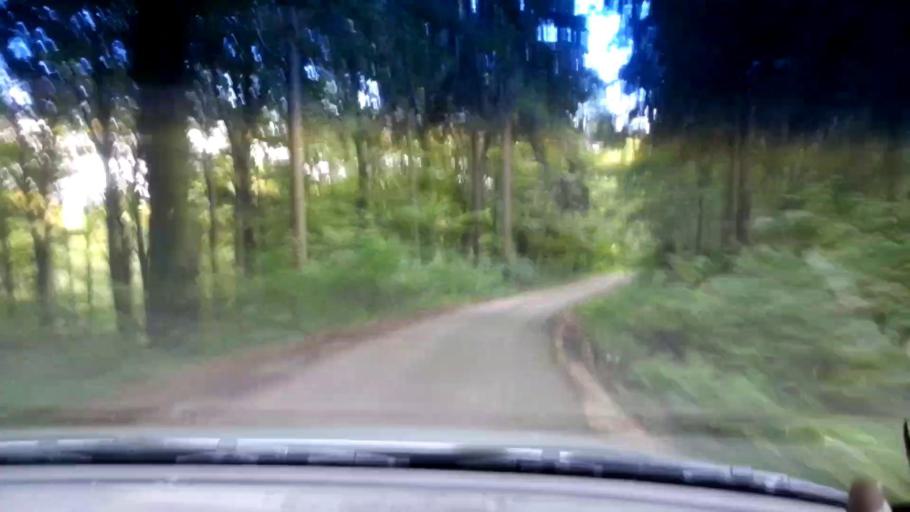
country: DE
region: Bavaria
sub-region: Upper Franconia
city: Schesslitz
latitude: 50.0157
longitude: 11.0361
